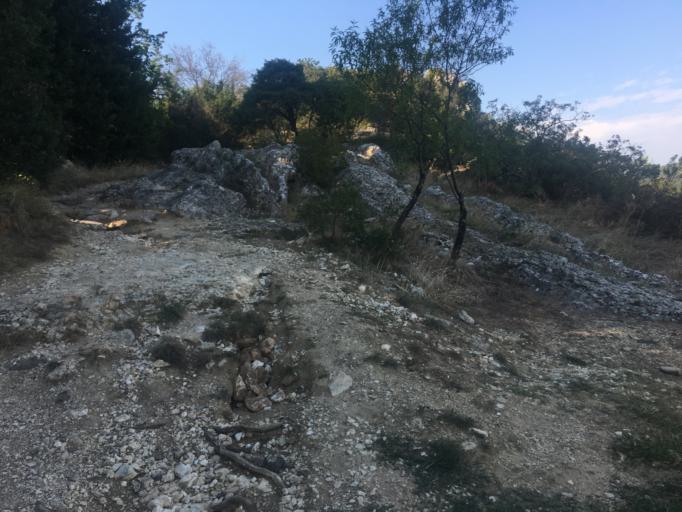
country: FR
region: Languedoc-Roussillon
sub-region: Departement du Gard
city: Saint-Julien-de-Peyrolas
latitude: 44.3052
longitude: 4.5548
